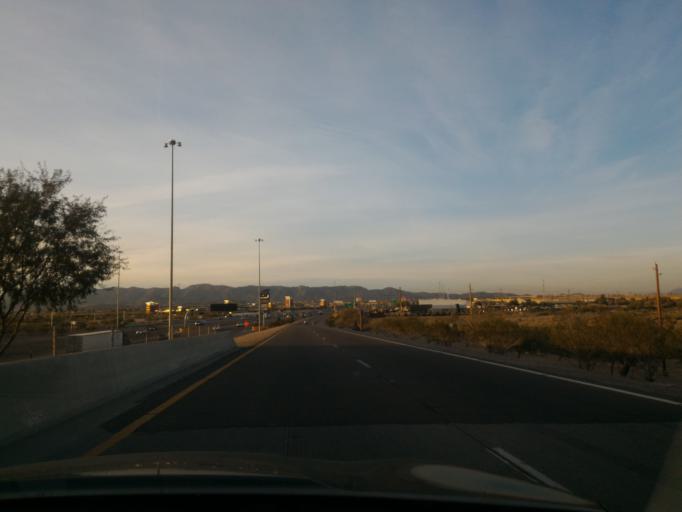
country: US
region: Arizona
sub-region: Maricopa County
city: Guadalupe
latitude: 33.2802
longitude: -111.9666
